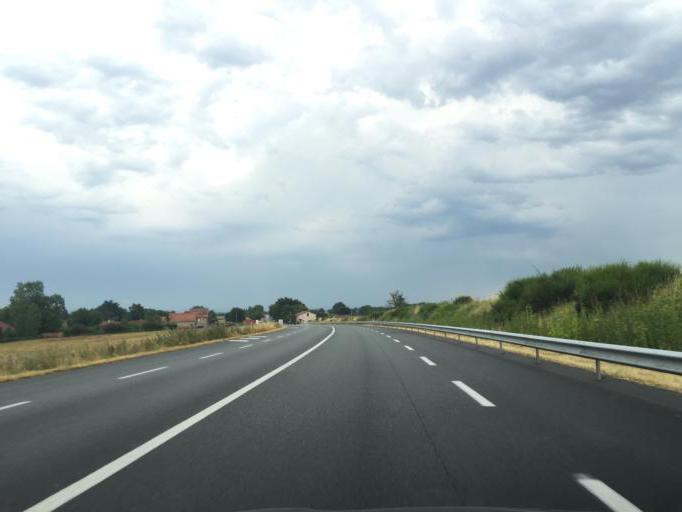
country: FR
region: Rhone-Alpes
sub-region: Departement de la Loire
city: Ambierle
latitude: 46.1322
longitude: 3.9044
